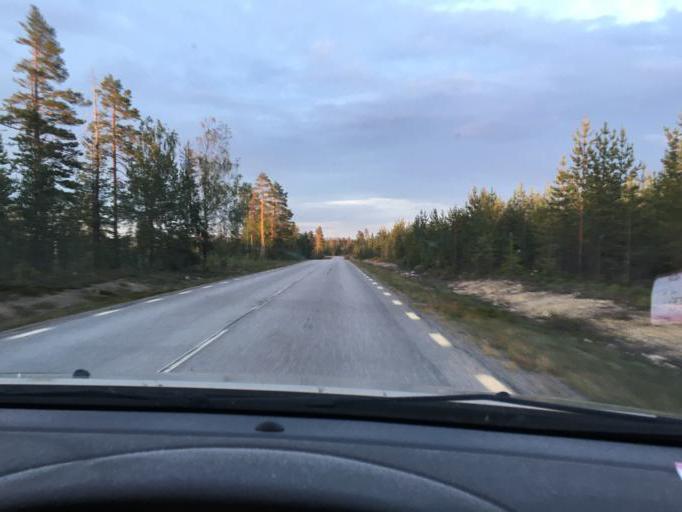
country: SE
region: Norrbotten
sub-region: Kalix Kommun
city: Toere
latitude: 66.0539
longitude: 22.4663
